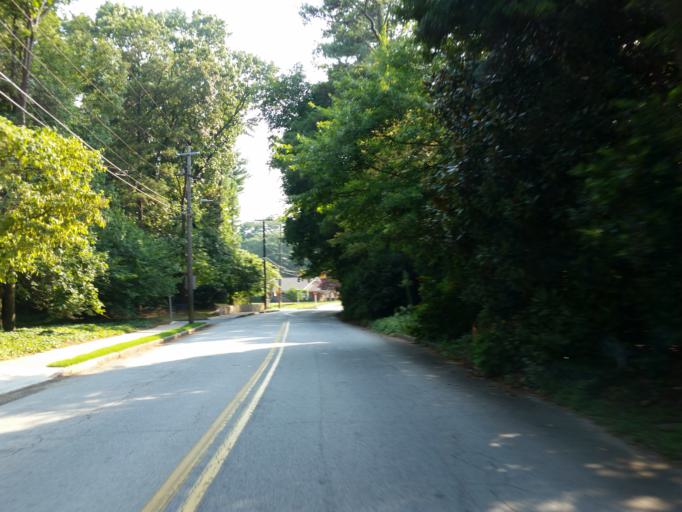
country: US
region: Georgia
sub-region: Cobb County
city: Vinings
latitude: 33.8452
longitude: -84.4063
